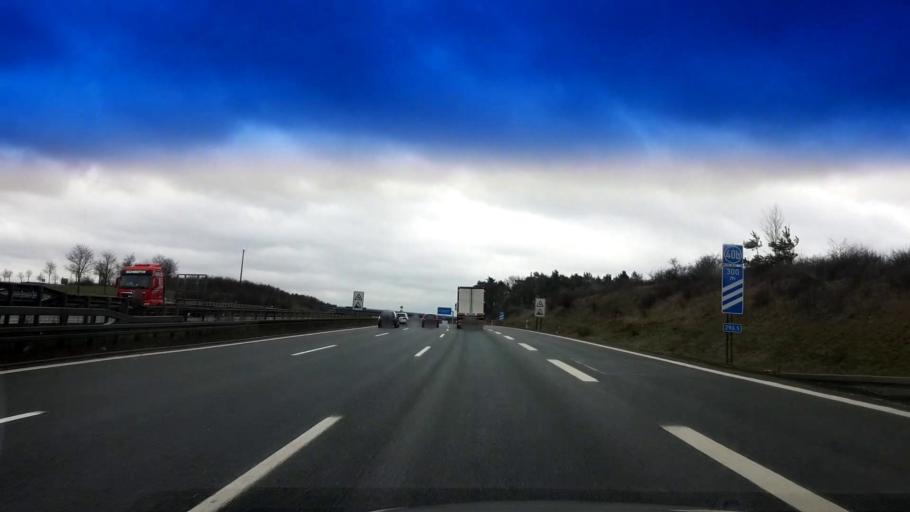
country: DE
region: Bavaria
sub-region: Upper Franconia
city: Bindlach
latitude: 50.0184
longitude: 11.6042
